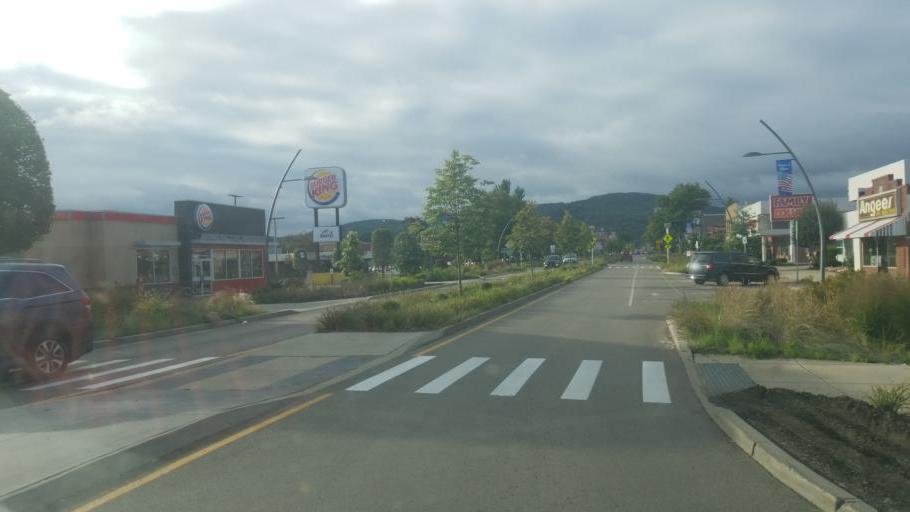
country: US
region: New York
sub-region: Cattaraugus County
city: Olean
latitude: 42.0851
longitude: -78.4300
